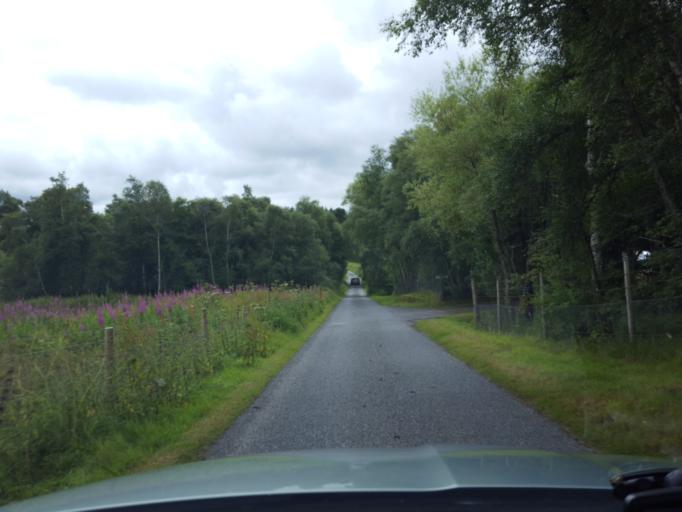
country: GB
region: Scotland
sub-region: Highland
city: Grantown on Spey
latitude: 57.3335
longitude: -3.5290
